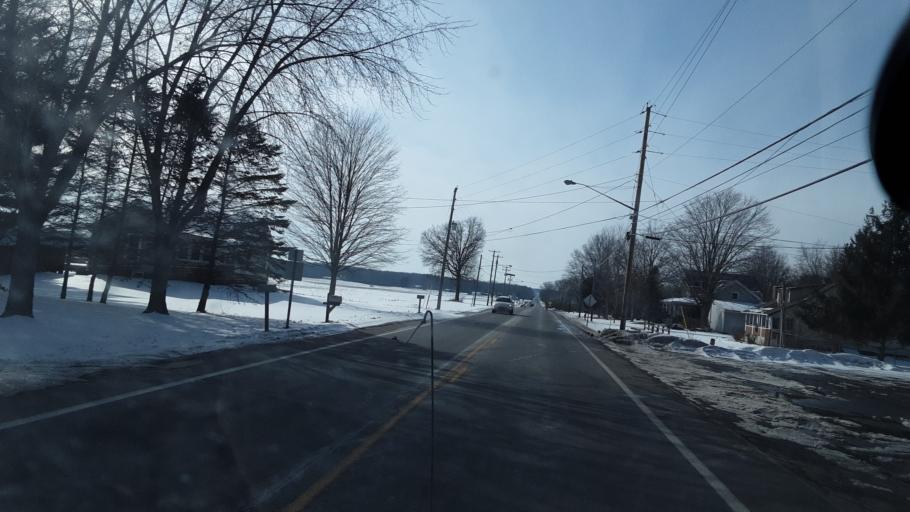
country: US
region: Ohio
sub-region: Mahoning County
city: Sebring
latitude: 41.0247
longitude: -81.0534
